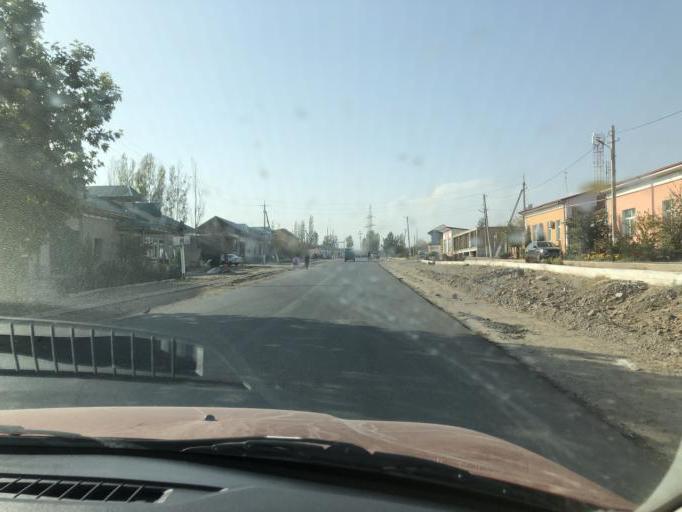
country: UZ
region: Namangan
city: Chust Shahri
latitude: 41.0737
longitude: 71.2023
